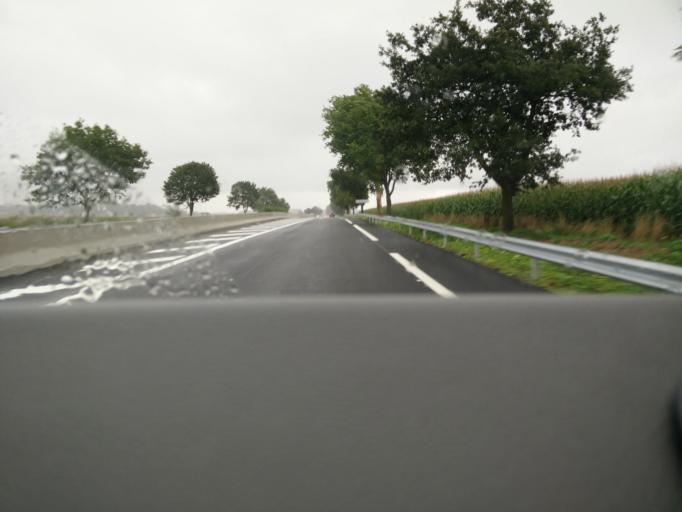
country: FR
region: Nord-Pas-de-Calais
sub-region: Departement du Pas-de-Calais
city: Saint-Pol-sur-Ternoise
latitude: 50.3637
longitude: 2.4393
